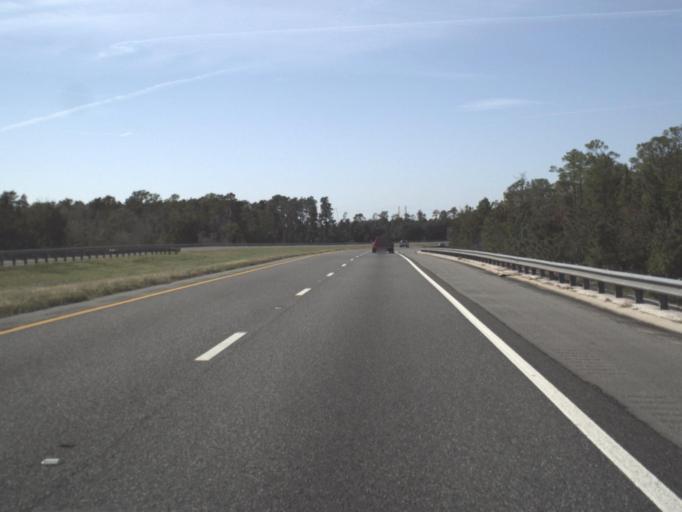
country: US
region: Florida
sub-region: Osceola County
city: Celebration
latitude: 28.3513
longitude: -81.4919
